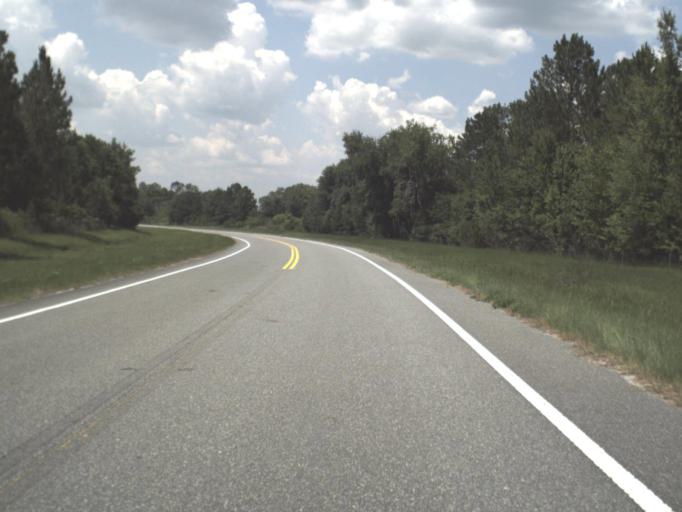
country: US
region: Florida
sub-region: Bradford County
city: Starke
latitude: 30.0165
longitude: -82.0495
